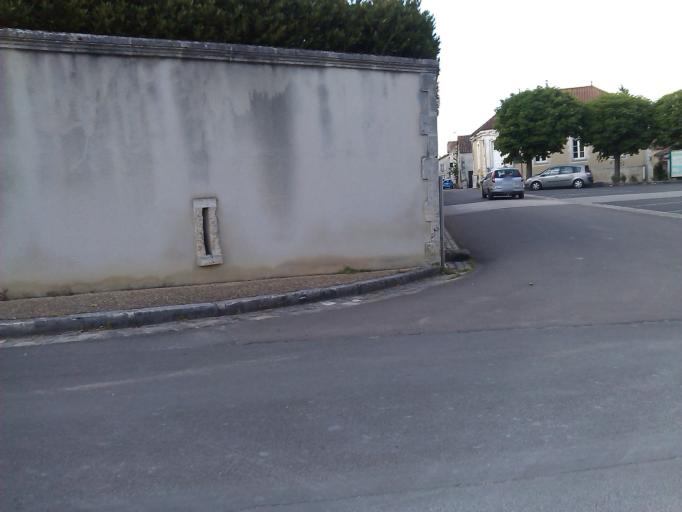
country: FR
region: Poitou-Charentes
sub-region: Departement de la Charente
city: Saint-Amant-de-Boixe
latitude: 45.7965
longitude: 0.1335
